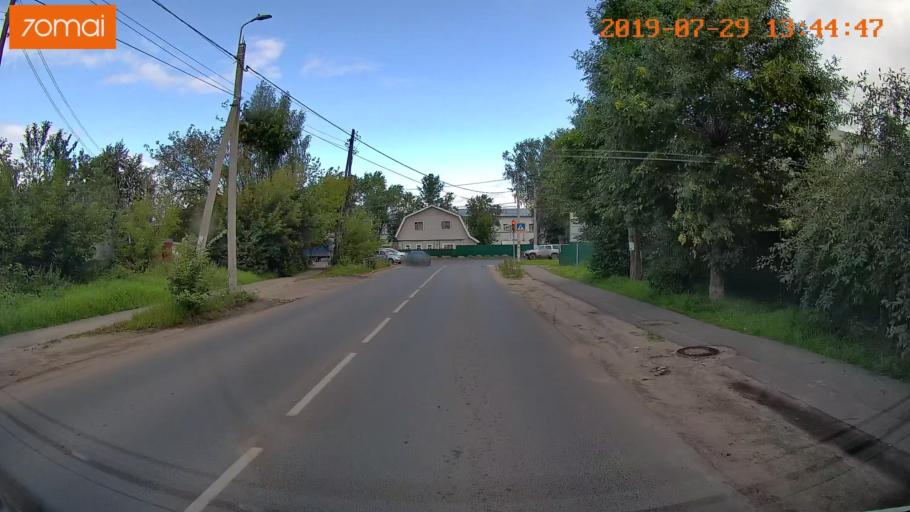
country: RU
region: Ivanovo
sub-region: Gorod Ivanovo
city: Ivanovo
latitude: 57.0114
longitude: 40.9368
